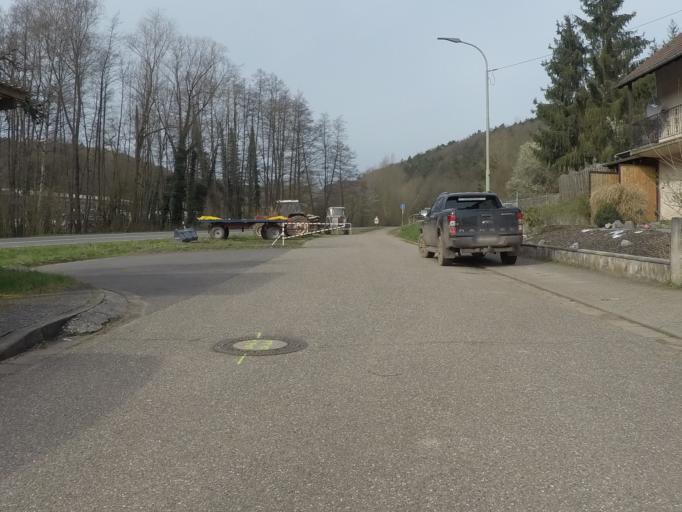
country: DE
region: Rheinland-Pfalz
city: Waldhambach
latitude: 49.1652
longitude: 7.9856
